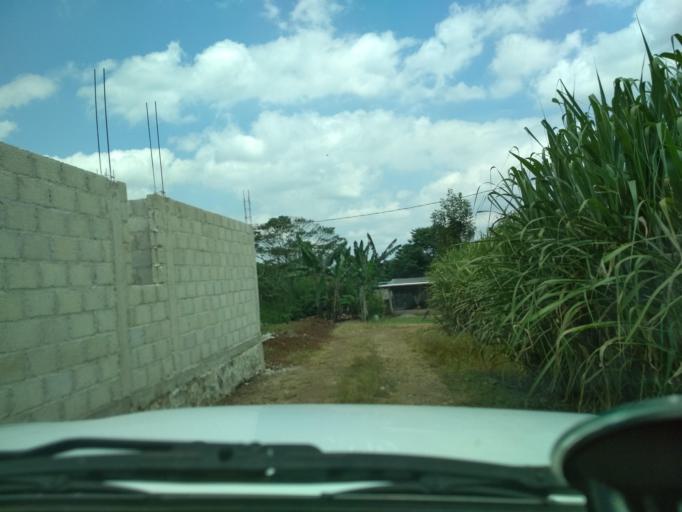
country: MX
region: Veracruz
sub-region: Fortin
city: Monte Salas
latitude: 18.9413
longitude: -97.0148
